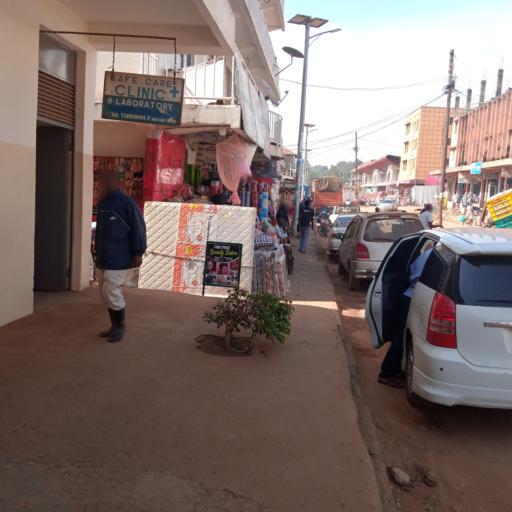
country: UG
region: Central Region
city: Masaka
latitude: -0.3449
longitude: 31.7386
